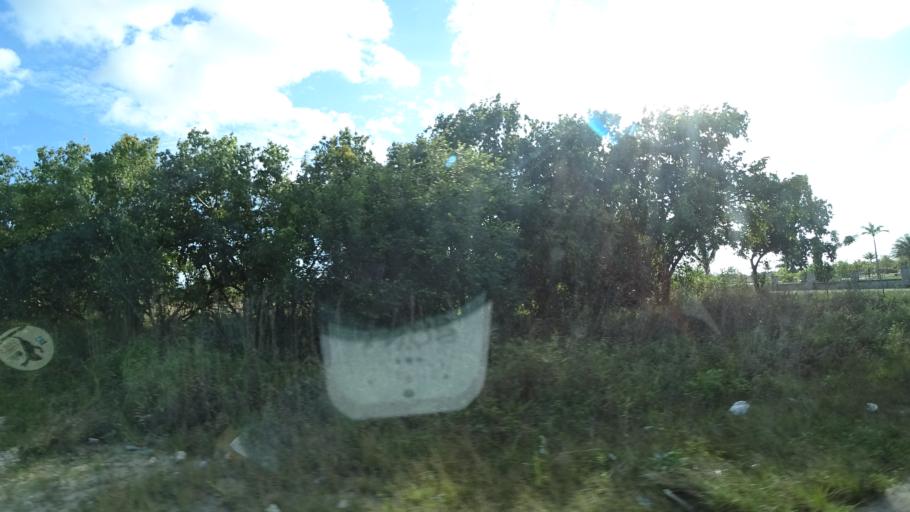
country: BZ
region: Belize
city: Belize City
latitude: 17.5687
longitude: -88.4133
